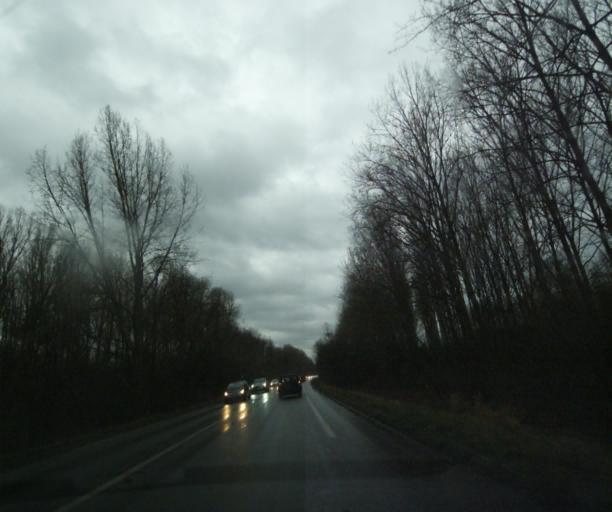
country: FR
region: Nord-Pas-de-Calais
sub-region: Departement du Nord
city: Vicq
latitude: 50.4065
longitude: 3.5822
